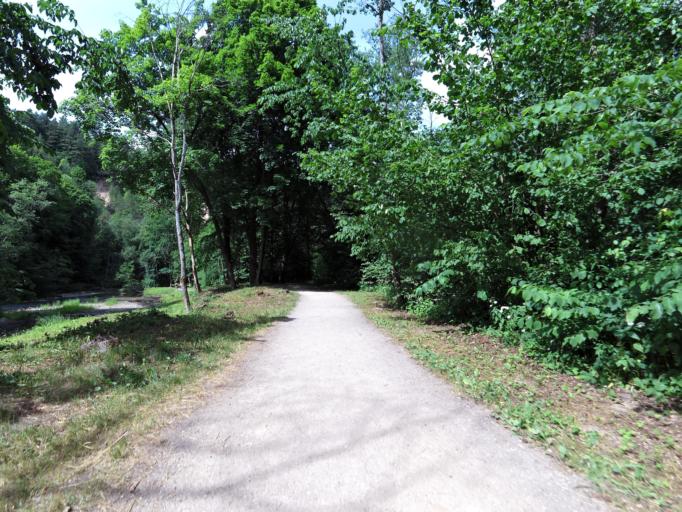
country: LT
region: Vilnius County
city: Rasos
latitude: 54.6900
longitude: 25.3529
